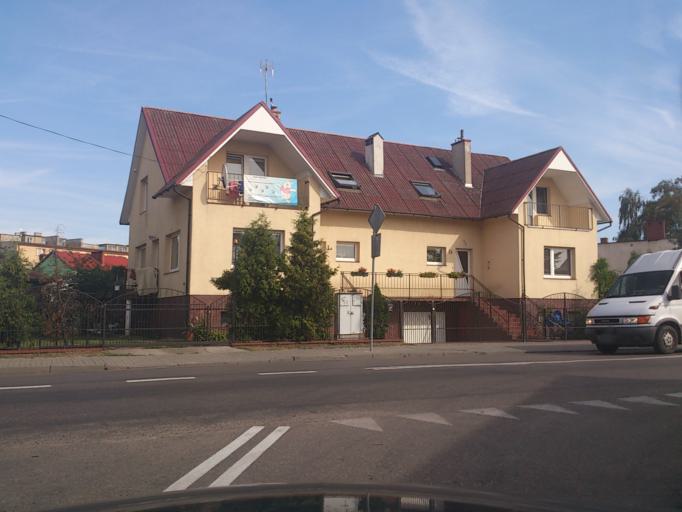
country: PL
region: Kujawsko-Pomorskie
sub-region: Powiat golubsko-dobrzynski
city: Golub-Dobrzyn
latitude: 53.1076
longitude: 19.0512
